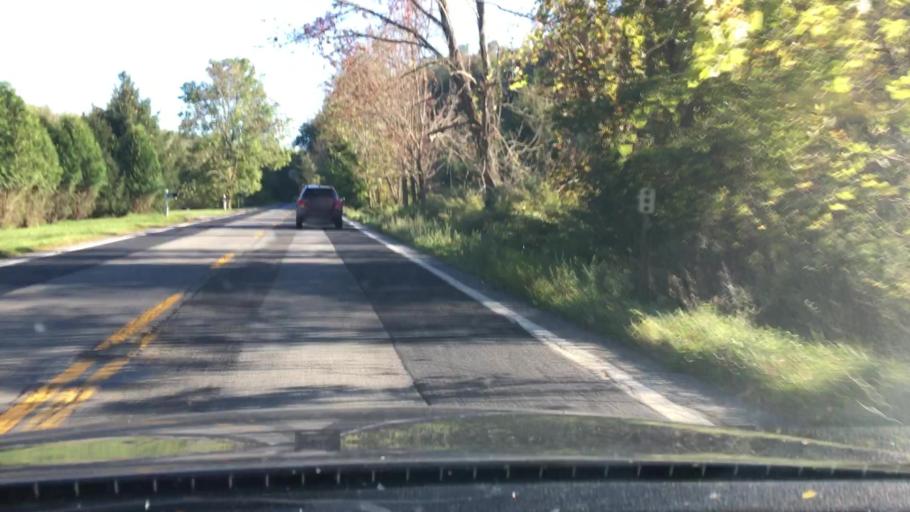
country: US
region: Connecticut
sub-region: Fairfield County
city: Sherman
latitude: 41.6497
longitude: -73.5293
